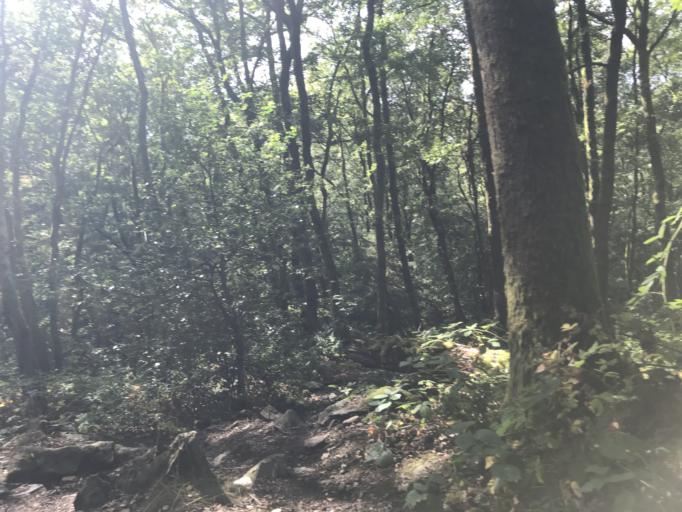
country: FR
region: Champagne-Ardenne
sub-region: Departement des Ardennes
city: Thilay
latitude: 49.8819
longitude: 4.7835
